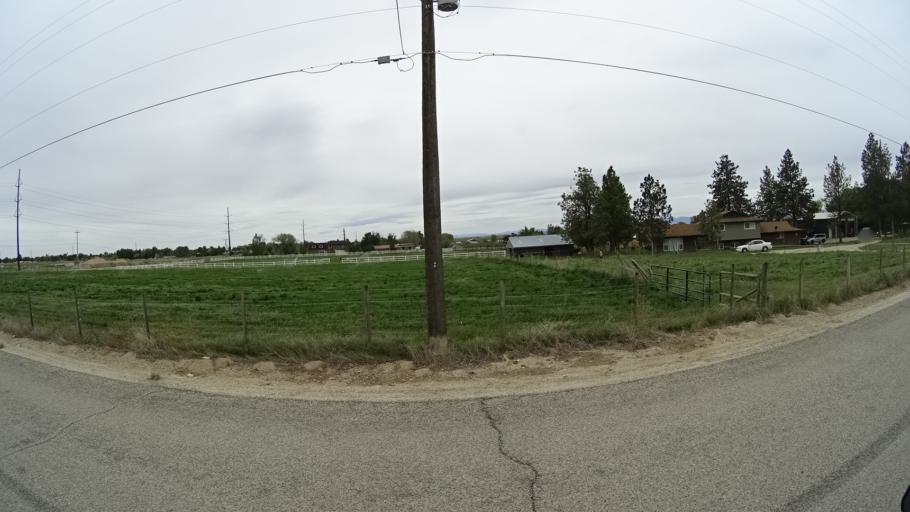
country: US
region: Idaho
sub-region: Ada County
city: Kuna
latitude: 43.4938
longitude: -116.3358
